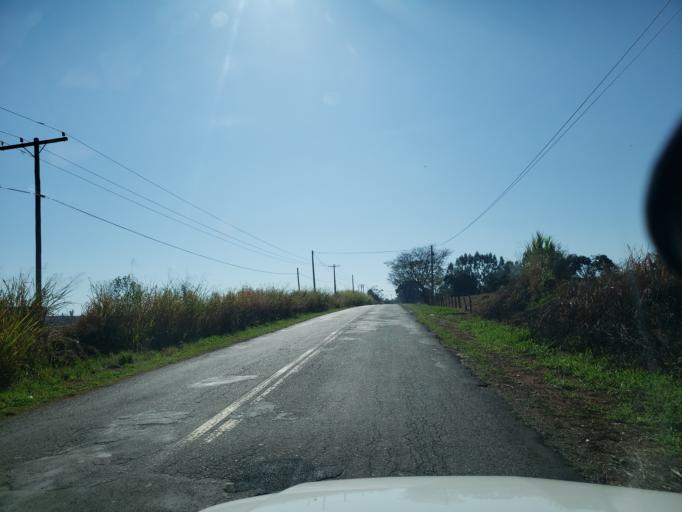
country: BR
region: Sao Paulo
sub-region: Moji-Guacu
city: Mogi-Gaucu
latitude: -22.3498
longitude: -46.8954
